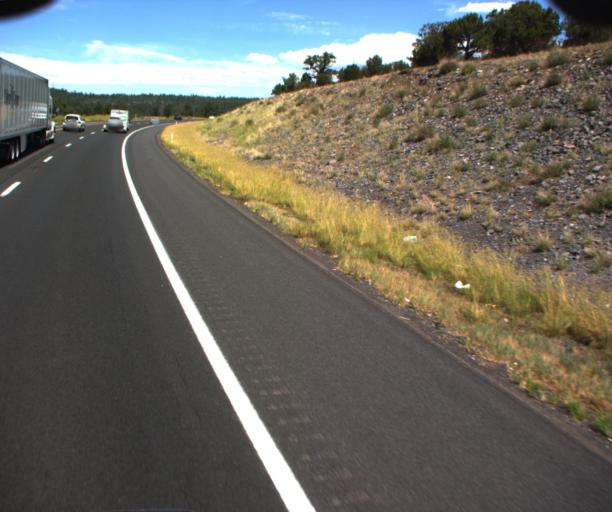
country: US
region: Arizona
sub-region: Yavapai County
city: Village of Oak Creek (Big Park)
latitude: 34.8129
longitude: -111.6100
